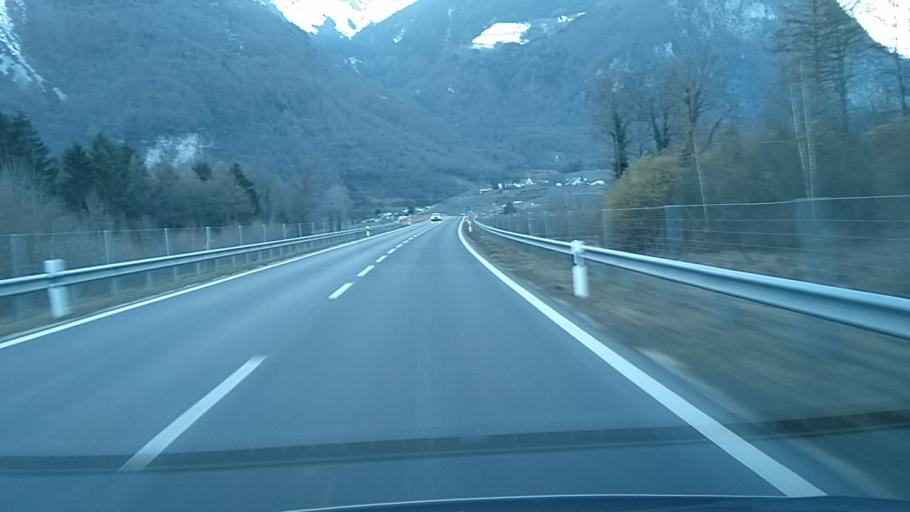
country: CH
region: Valais
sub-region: Monthey District
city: Port-Valais
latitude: 46.3571
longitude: 6.8862
